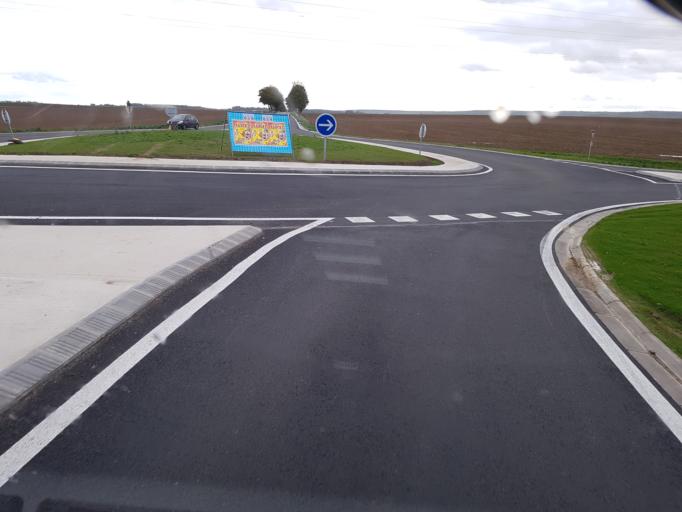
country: FR
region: Picardie
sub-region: Departement de l'Oise
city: Le Plessis-Belleville
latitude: 49.0855
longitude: 2.7568
